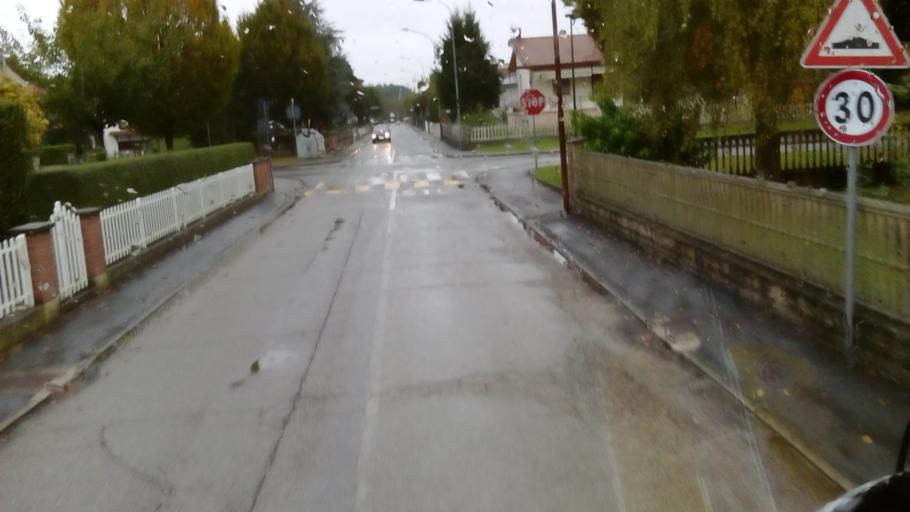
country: IT
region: Emilia-Romagna
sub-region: Provincia di Reggio Emilia
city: Luzzara
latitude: 44.9565
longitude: 10.6924
